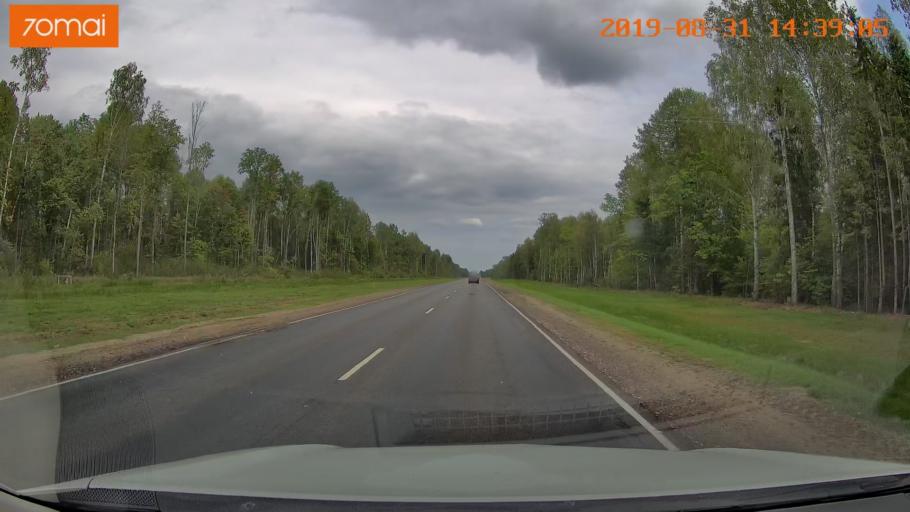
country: RU
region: Smolensk
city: Yekimovichi
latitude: 54.1890
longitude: 33.5437
